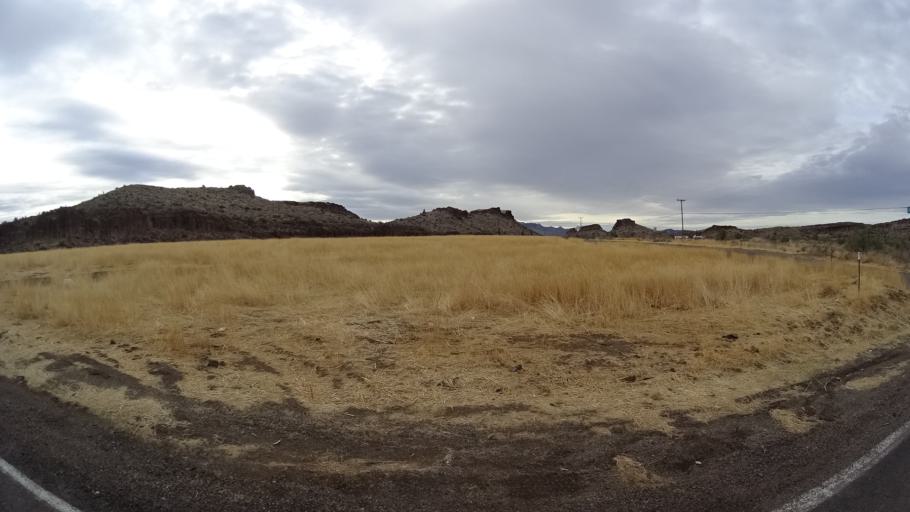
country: US
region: Arizona
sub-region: Mohave County
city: Kingman
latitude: 35.2179
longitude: -114.0704
